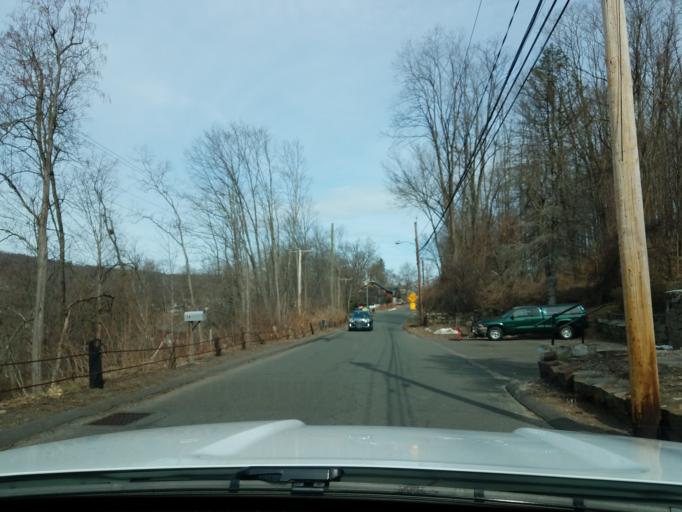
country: US
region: Connecticut
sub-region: Hartford County
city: Collinsville
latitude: 41.8071
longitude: -72.9189
